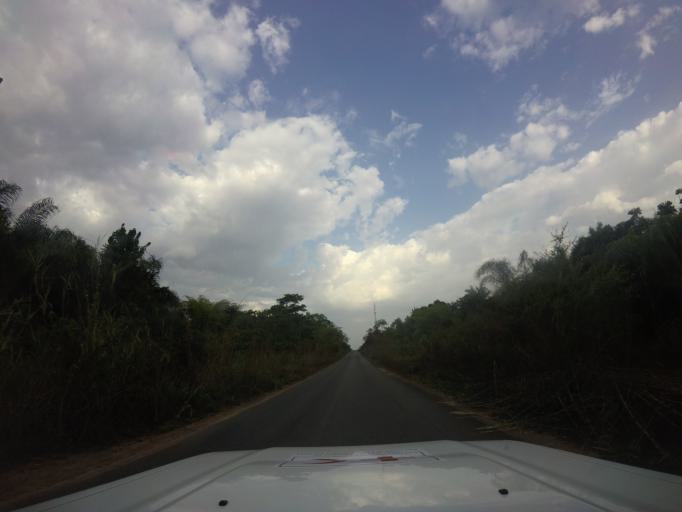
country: LR
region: Bomi
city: Tubmanburg
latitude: 6.6903
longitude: -10.8851
